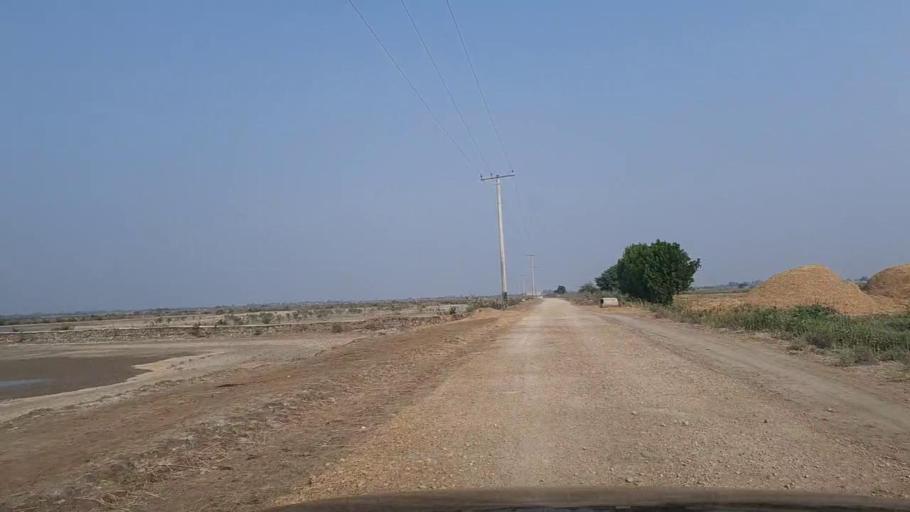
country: PK
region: Sindh
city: Thatta
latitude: 24.7510
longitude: 67.8725
